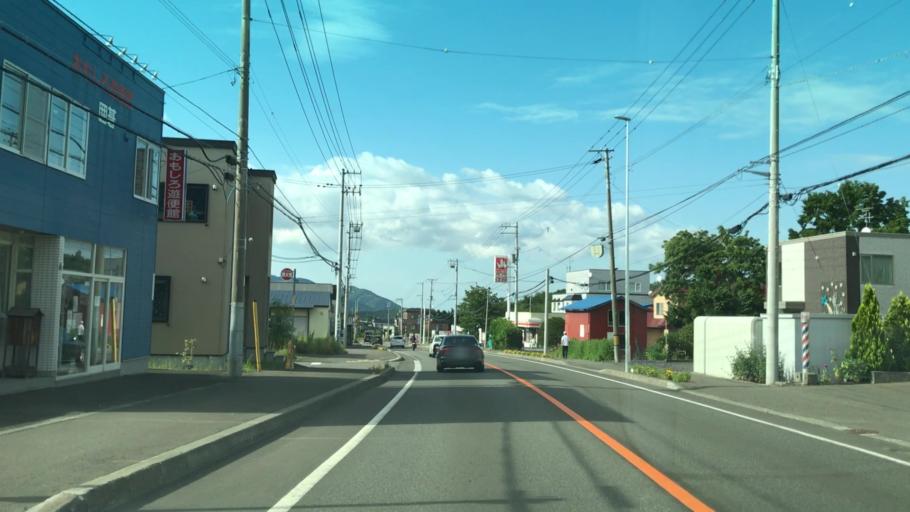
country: JP
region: Hokkaido
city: Sapporo
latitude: 42.9488
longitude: 141.3469
